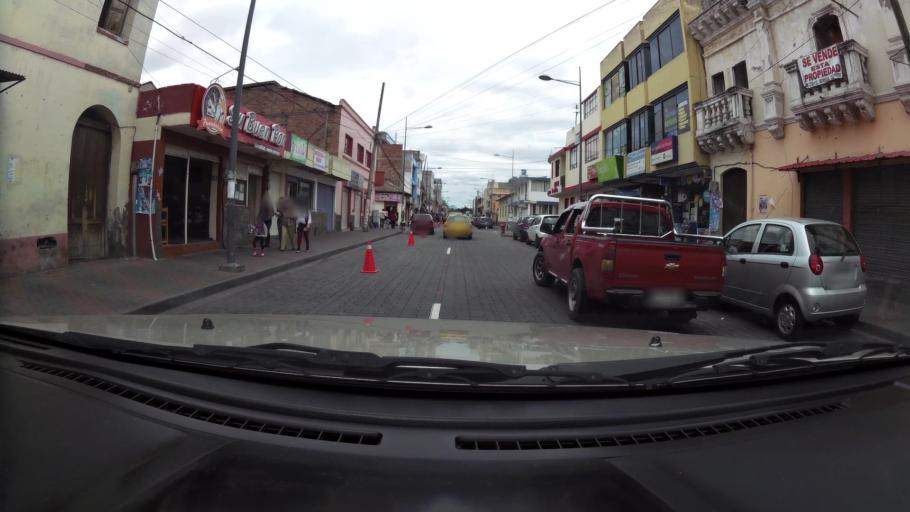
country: EC
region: Cotopaxi
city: San Miguel de Salcedo
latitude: -1.0399
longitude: -78.5907
